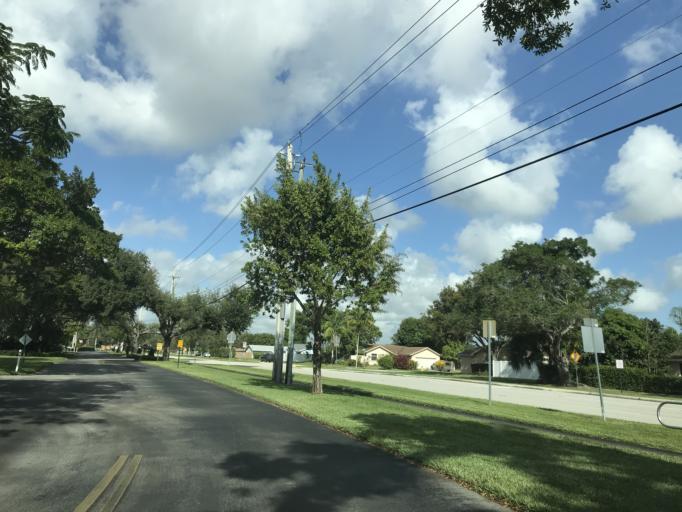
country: US
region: Florida
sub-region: Broward County
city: Coconut Creek
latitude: 26.2603
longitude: -80.1950
